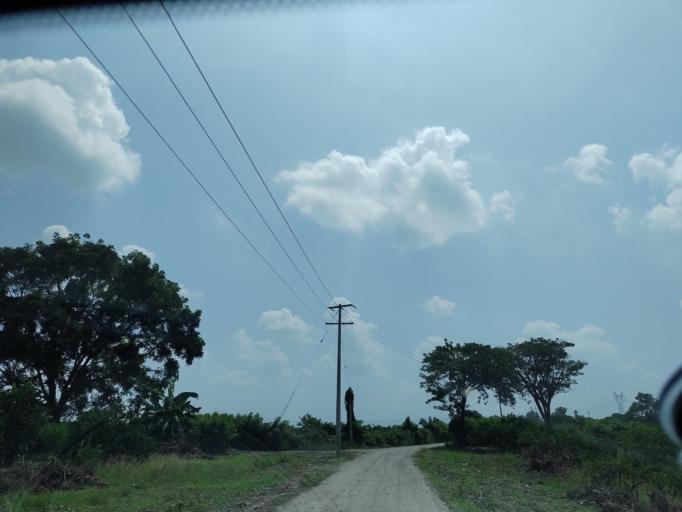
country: MX
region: Veracruz
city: Martinez de la Torre
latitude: 20.0878
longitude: -97.0378
